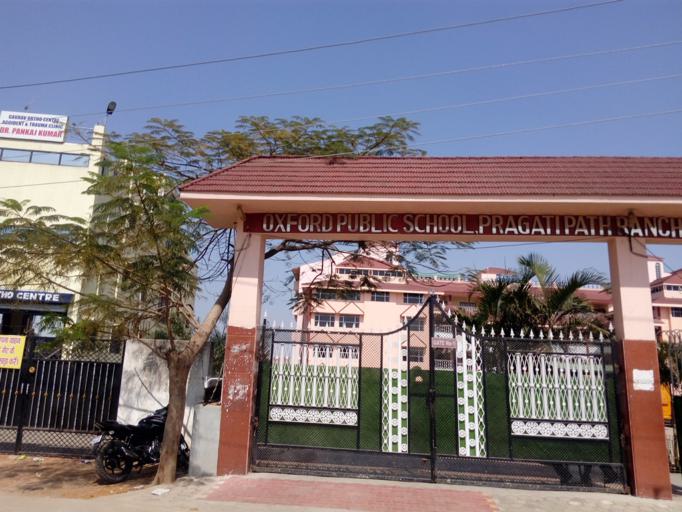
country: IN
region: Jharkhand
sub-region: Ranchi
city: Ranchi
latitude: 23.3544
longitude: 85.3508
